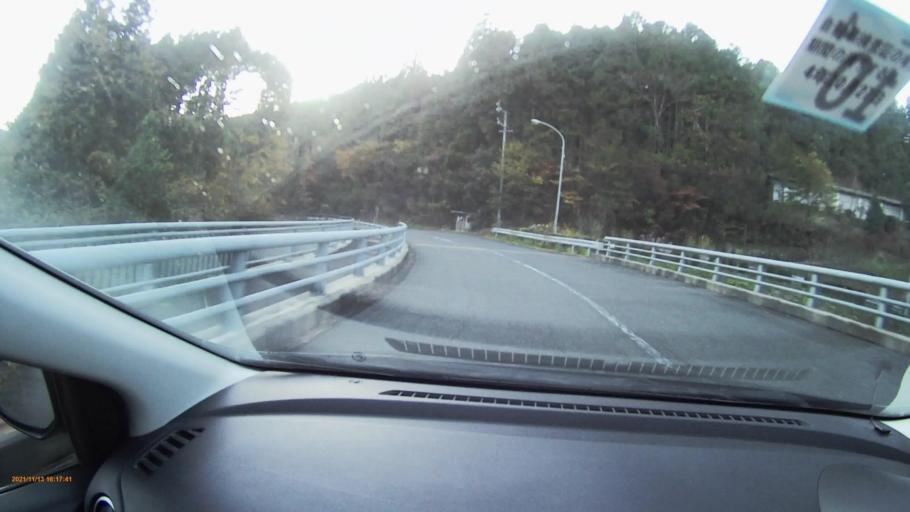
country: JP
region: Gifu
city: Nakatsugawa
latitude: 35.5793
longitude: 137.5020
